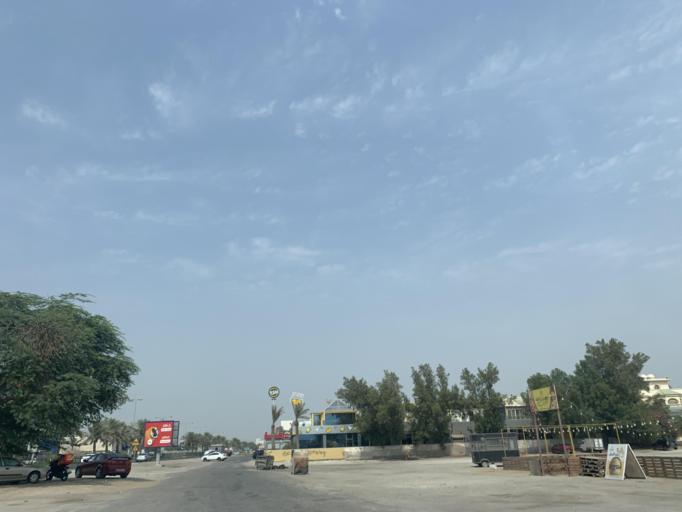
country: BH
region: Manama
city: Jidd Hafs
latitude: 26.2178
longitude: 50.4842
